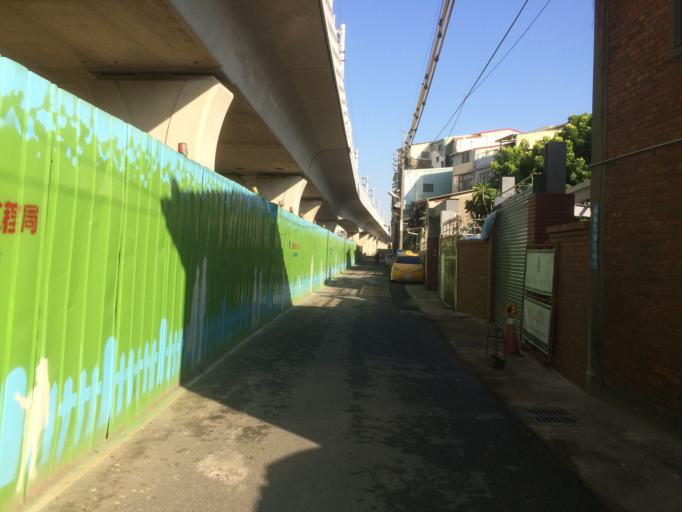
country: TW
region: Taiwan
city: Fengyuan
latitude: 24.2142
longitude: 120.7062
